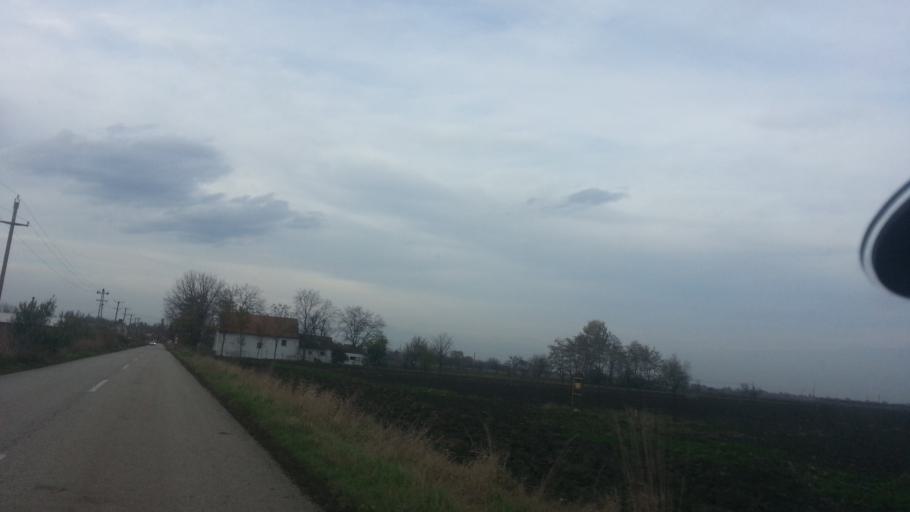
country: RS
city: Putinci
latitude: 44.9777
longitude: 19.9701
